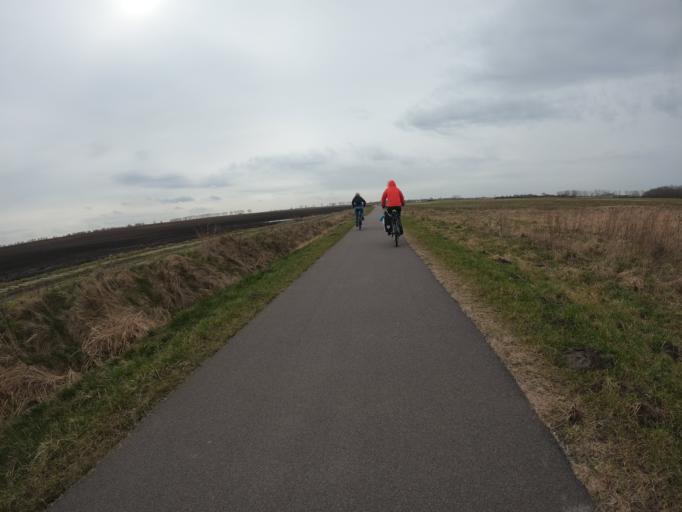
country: PL
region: West Pomeranian Voivodeship
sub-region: Powiat gryficki
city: Mrzezyno
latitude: 54.1080
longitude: 15.2928
